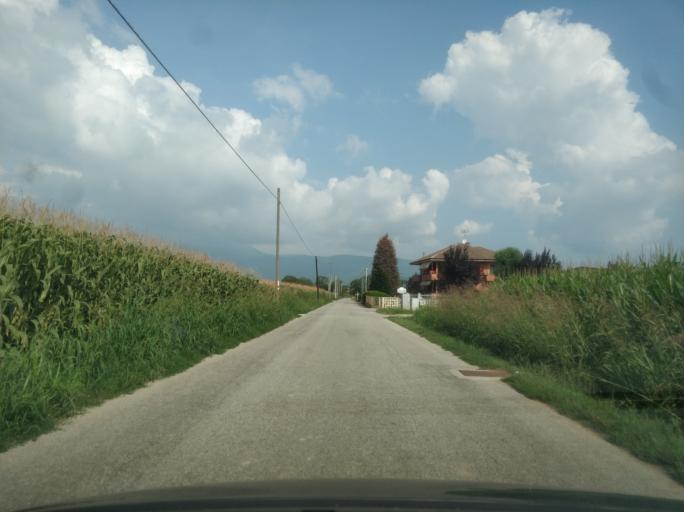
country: IT
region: Piedmont
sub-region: Provincia di Cuneo
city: Caraglio
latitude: 44.4330
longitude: 7.4323
